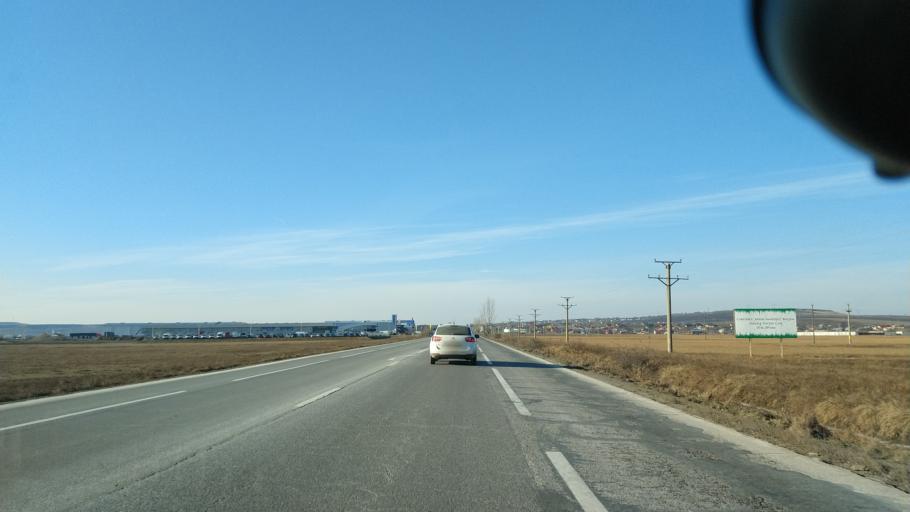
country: RO
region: Iasi
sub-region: Comuna Letcani
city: Letcani
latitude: 47.1876
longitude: 27.4415
